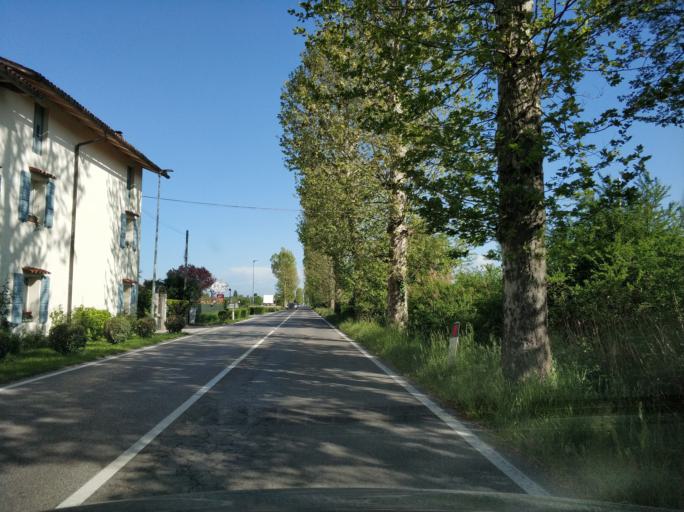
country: IT
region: Friuli Venezia Giulia
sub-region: Provincia di Udine
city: Terzo d'Aquileia
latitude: 45.7893
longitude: 13.3571
